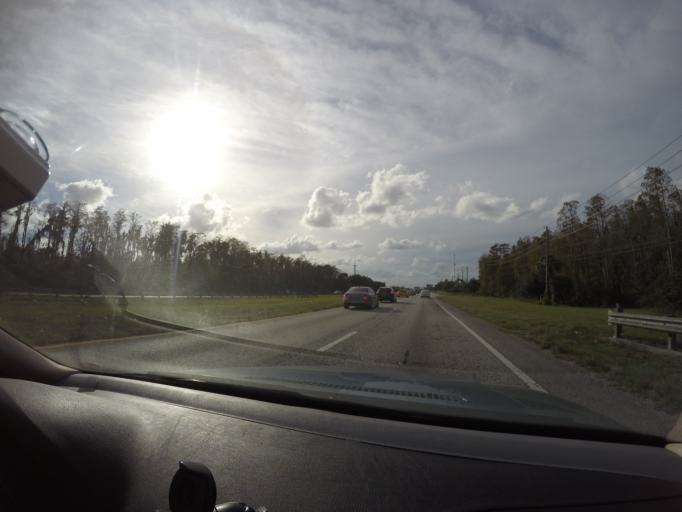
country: US
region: Florida
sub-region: Orange County
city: Tangelo Park
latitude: 28.4504
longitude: -81.4350
